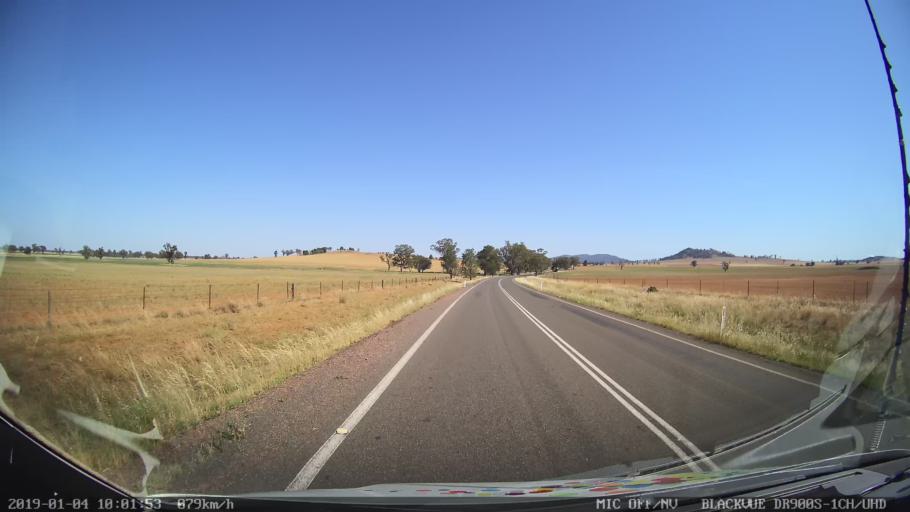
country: AU
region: New South Wales
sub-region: Cabonne
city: Canowindra
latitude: -33.4829
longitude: 148.3670
